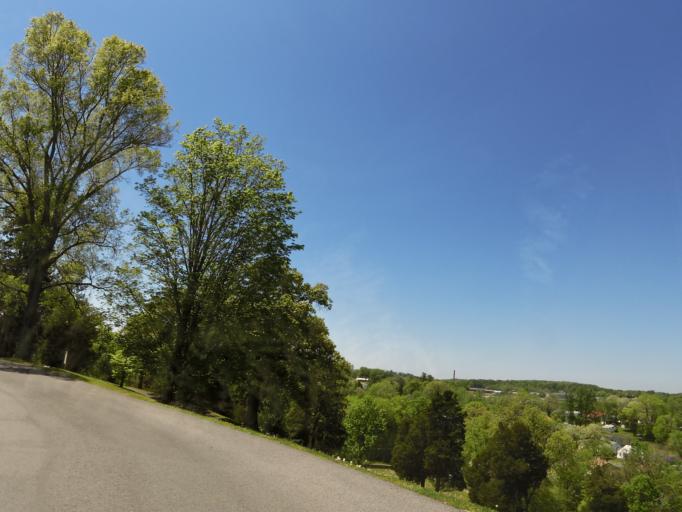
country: US
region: Tennessee
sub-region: Greene County
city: Greeneville
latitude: 36.1558
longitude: -82.8377
